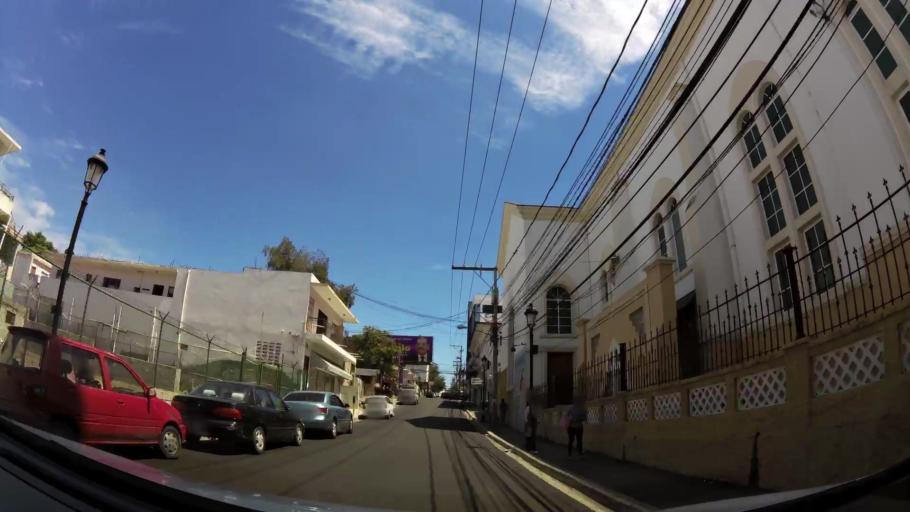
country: DO
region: Santiago
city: Santiago de los Caballeros
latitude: 19.4504
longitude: -70.6992
